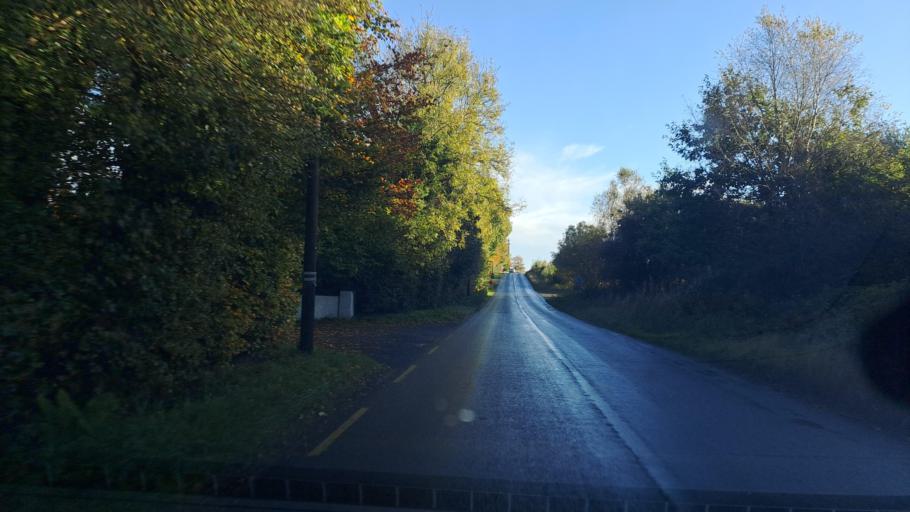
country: IE
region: Ulster
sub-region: An Cabhan
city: Cootehill
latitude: 54.1040
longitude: -7.0734
